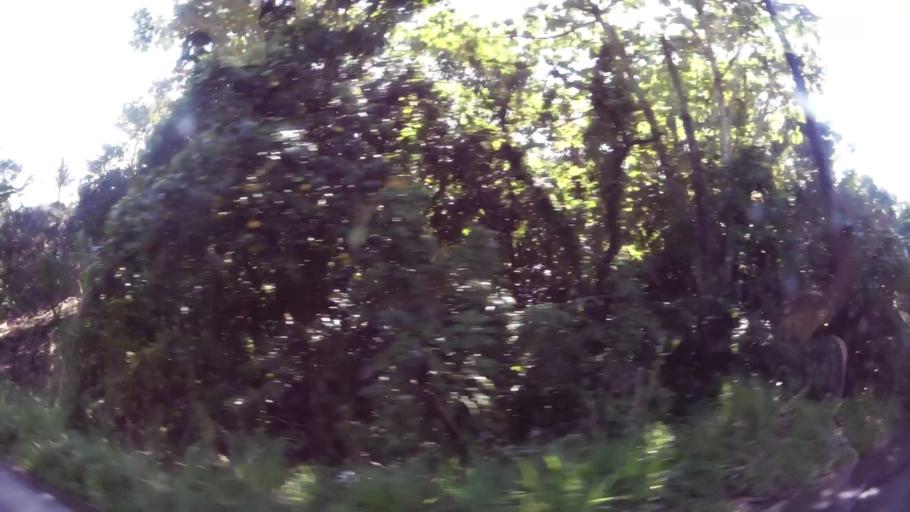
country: DM
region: Saint Paul
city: Pont Casse
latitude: 15.3584
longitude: -61.3559
